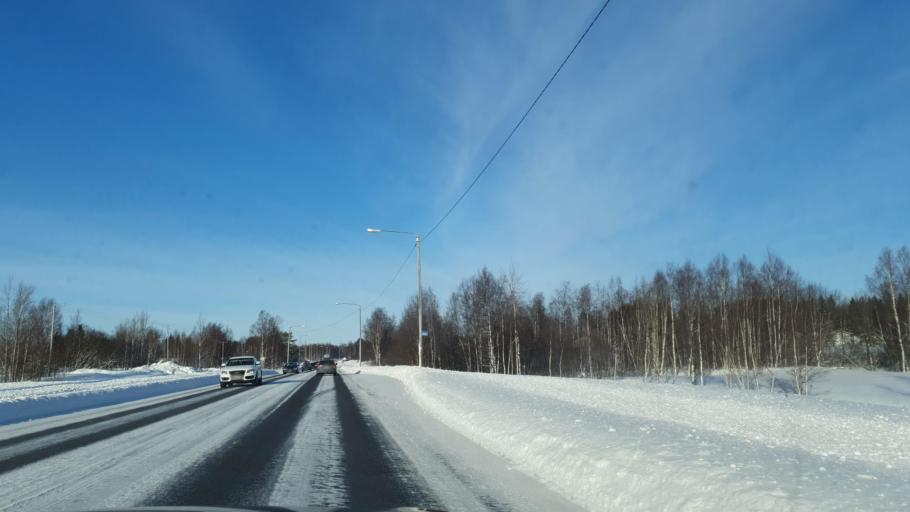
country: FI
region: Lapland
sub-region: Kemi-Tornio
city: Tornio
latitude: 65.8916
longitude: 24.1477
